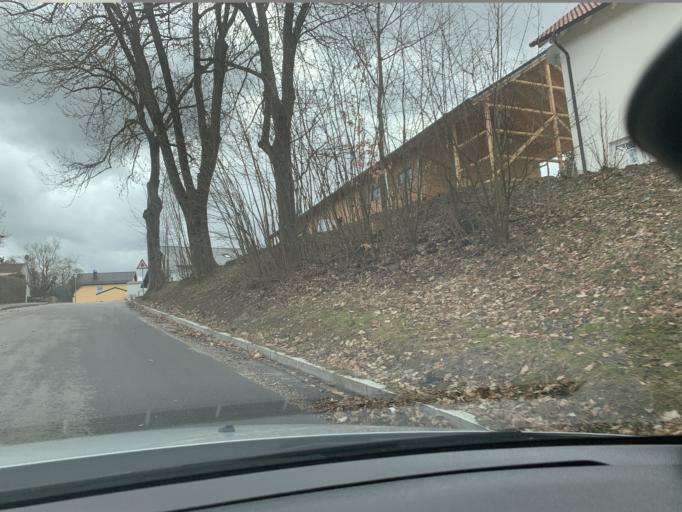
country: DE
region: Bavaria
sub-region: Lower Bavaria
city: Geisenhausen
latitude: 48.4714
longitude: 12.2618
